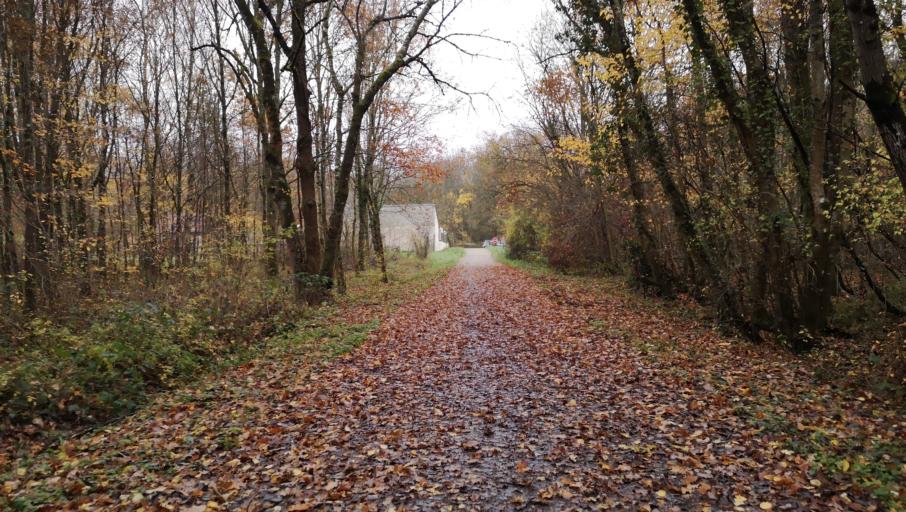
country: FR
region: Centre
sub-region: Departement du Loiret
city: Saint-Jean-de-Braye
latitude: 47.9328
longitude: 1.9865
